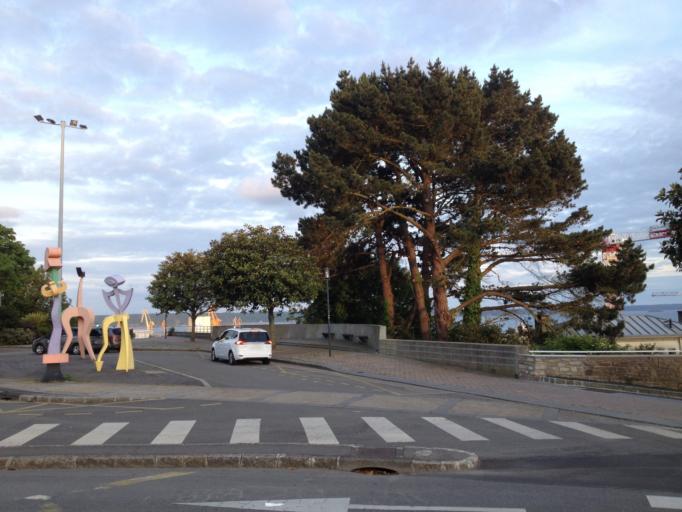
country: FR
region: Brittany
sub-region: Departement du Finistere
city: Brest
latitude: 48.3876
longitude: -4.4806
